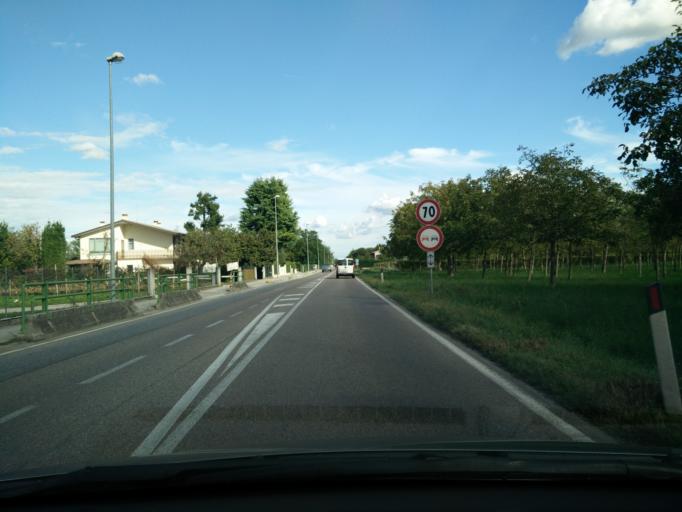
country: IT
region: Veneto
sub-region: Provincia di Treviso
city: Varago
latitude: 45.7407
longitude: 12.2967
